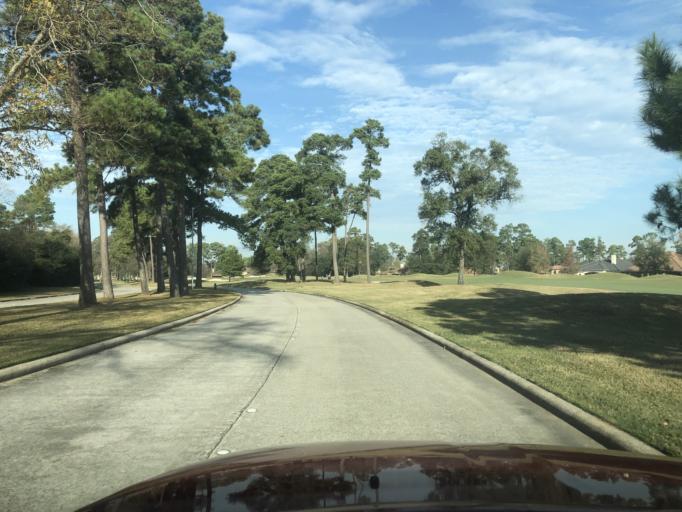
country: US
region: Texas
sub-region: Harris County
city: Spring
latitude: 30.0035
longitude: -95.4732
